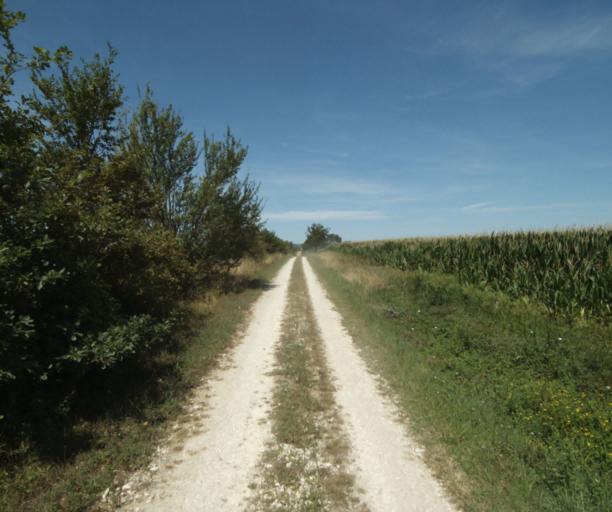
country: FR
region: Midi-Pyrenees
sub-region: Departement de la Haute-Garonne
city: Revel
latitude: 43.4997
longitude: 2.0156
